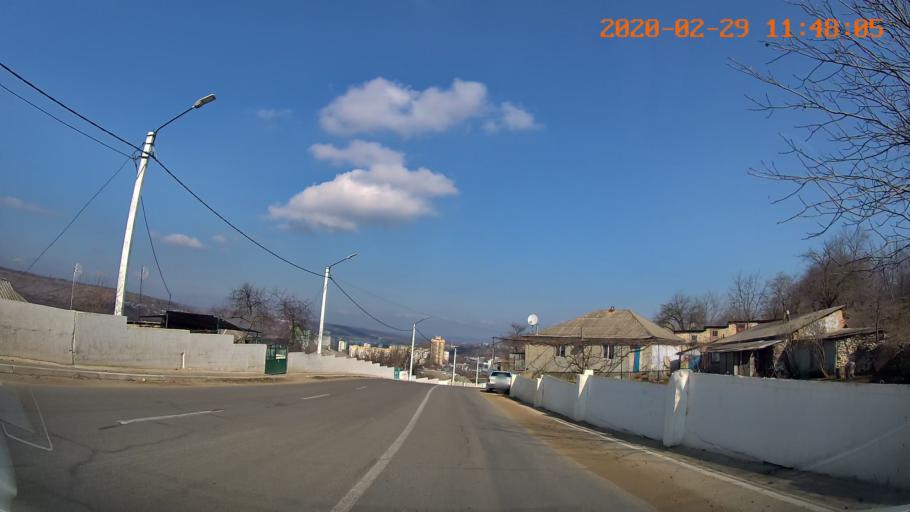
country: MD
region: Rezina
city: Rezina
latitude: 47.7458
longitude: 28.9889
